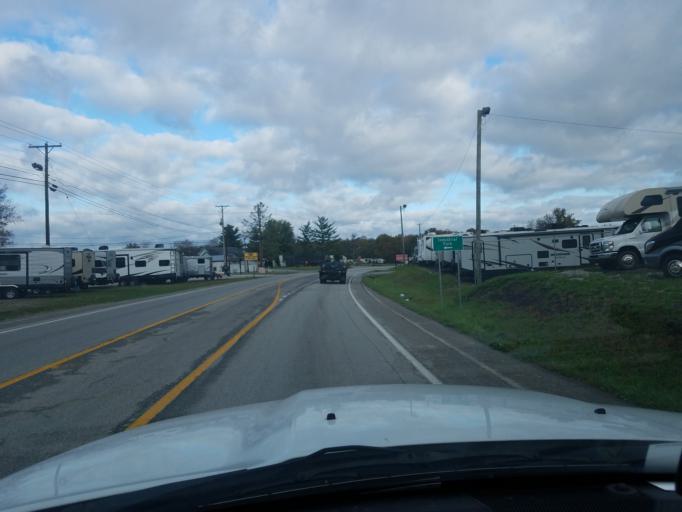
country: US
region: Kentucky
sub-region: Laurel County
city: London
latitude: 37.0648
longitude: -84.0574
